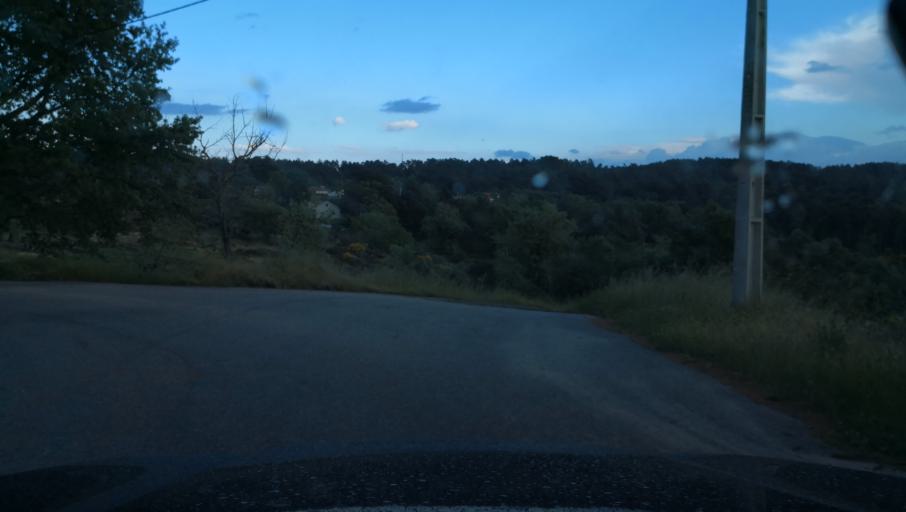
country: PT
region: Vila Real
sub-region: Vila Real
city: Vila Real
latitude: 41.3154
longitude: -7.6743
